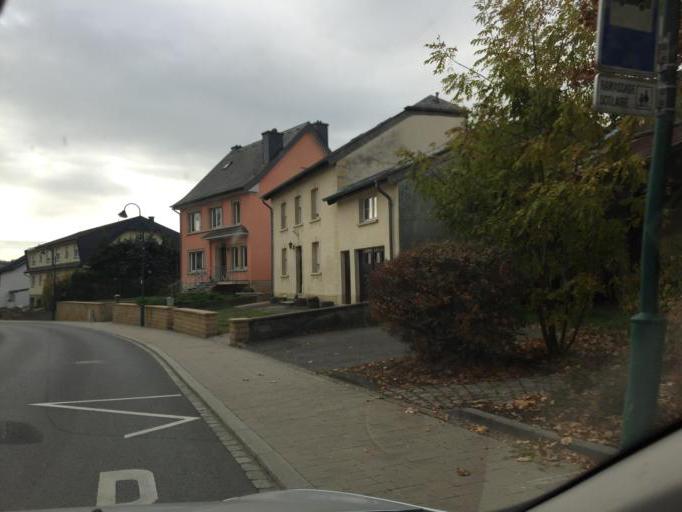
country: LU
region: Luxembourg
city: Capellen
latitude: 49.6168
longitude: 5.9865
